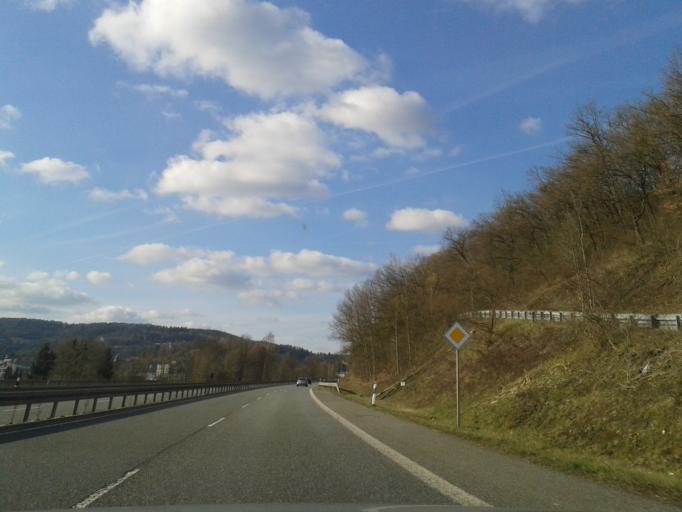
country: DE
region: Hesse
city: Herborn
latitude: 50.6732
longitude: 8.3125
